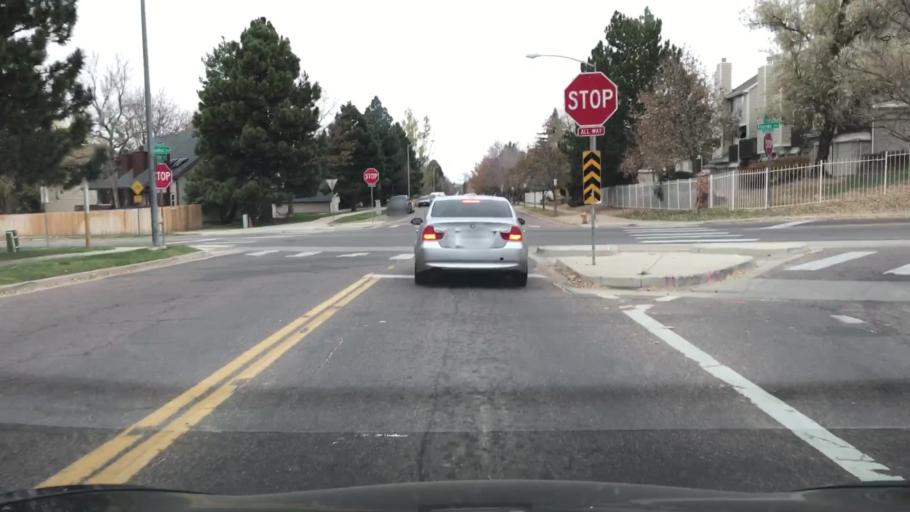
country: US
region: Colorado
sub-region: Arapahoe County
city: Glendale
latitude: 39.6891
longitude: -104.8965
